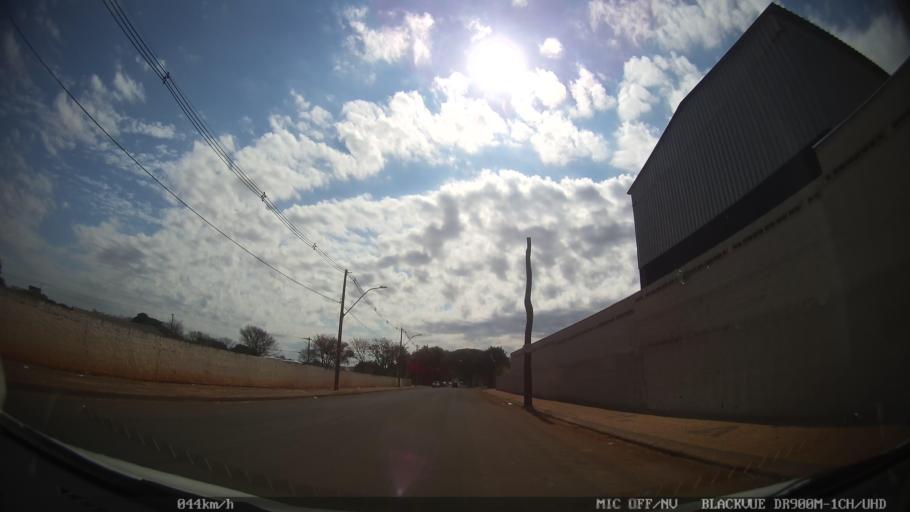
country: BR
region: Sao Paulo
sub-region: Americana
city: Americana
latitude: -22.7268
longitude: -47.3202
